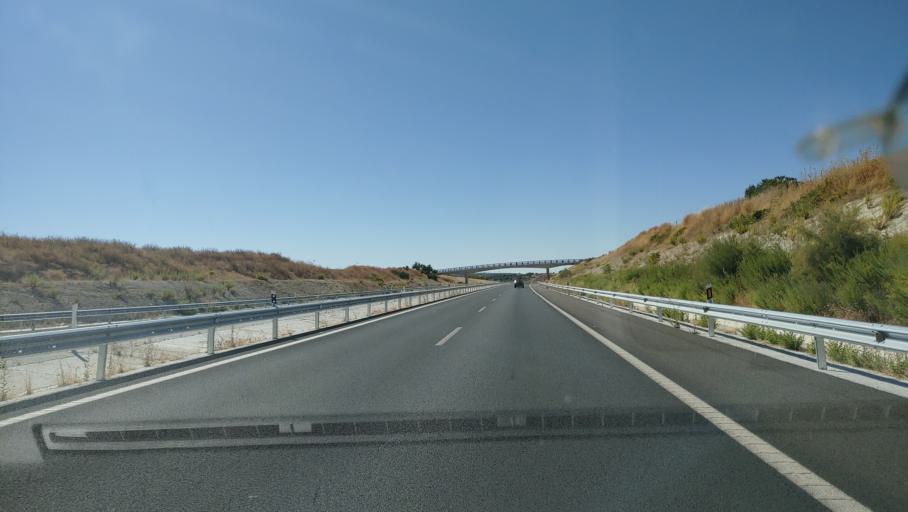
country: ES
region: Andalusia
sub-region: Provincia de Jaen
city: Torreperogil
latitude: 38.0422
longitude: -3.2709
